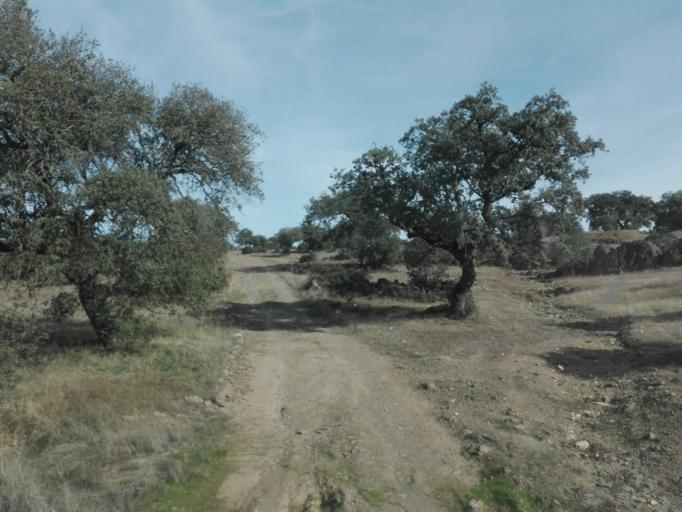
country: ES
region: Extremadura
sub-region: Provincia de Badajoz
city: Valverde de Llerena
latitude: 38.2172
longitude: -5.7437
